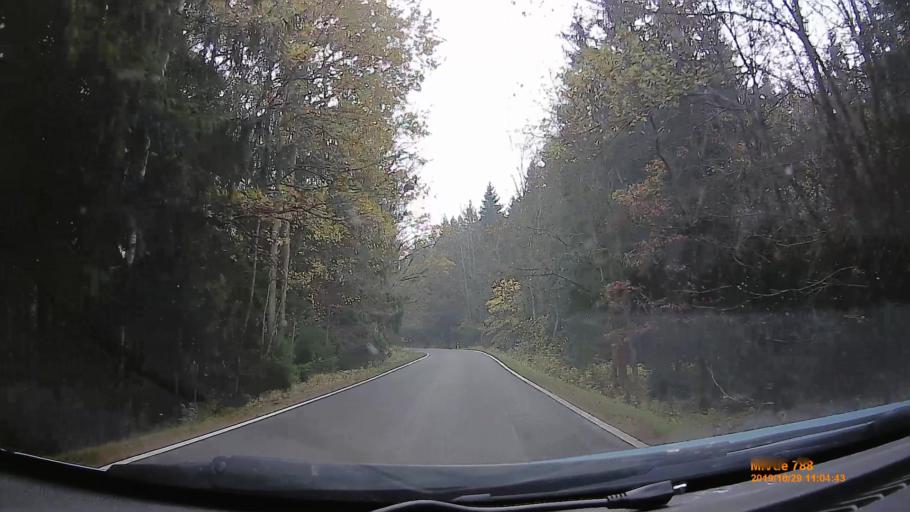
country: PL
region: Lower Silesian Voivodeship
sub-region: Powiat klodzki
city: Szczytna
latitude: 50.4753
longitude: 16.4676
